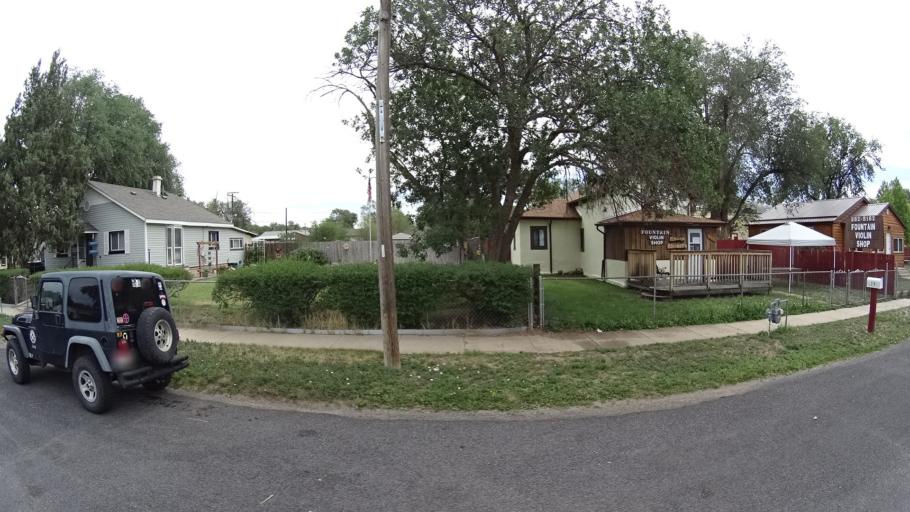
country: US
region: Colorado
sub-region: El Paso County
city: Fountain
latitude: 38.6844
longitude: -104.7006
